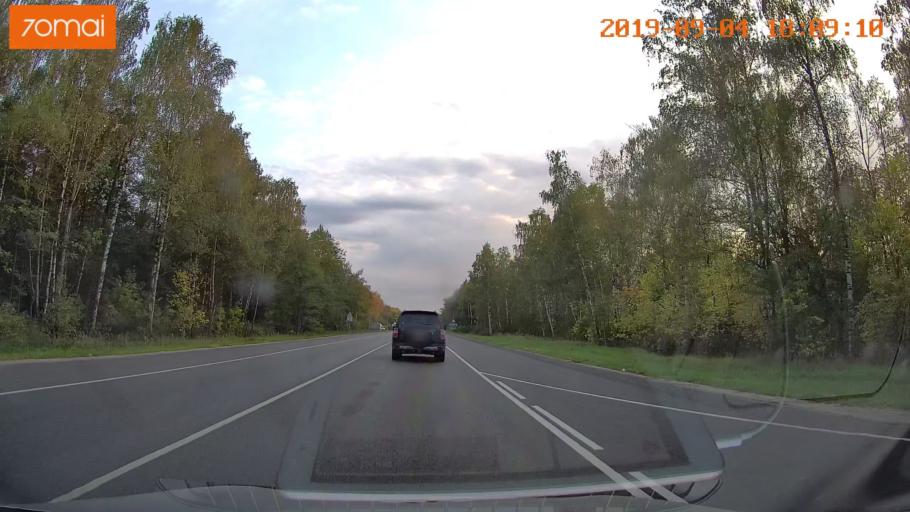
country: RU
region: Moskovskaya
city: Khorlovo
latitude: 55.3983
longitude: 38.7773
